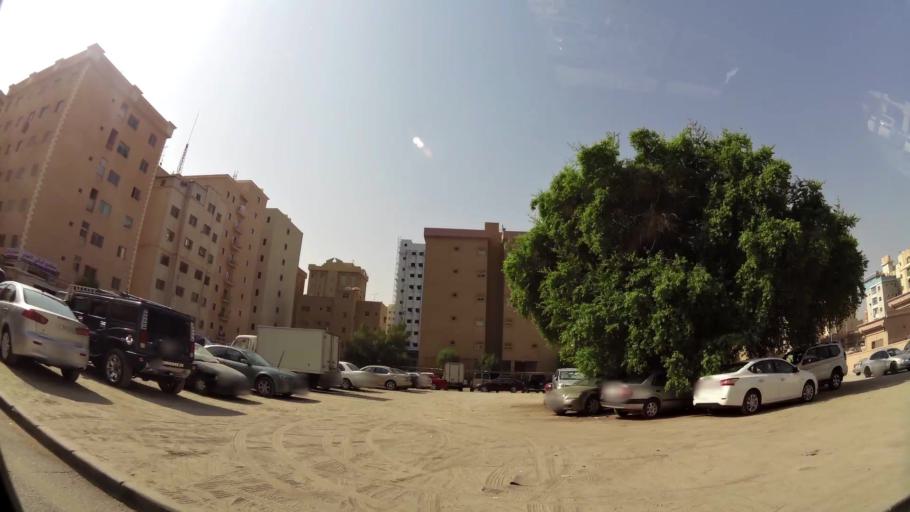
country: KW
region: Muhafazat Hawalli
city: Hawalli
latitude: 29.3368
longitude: 48.0319
